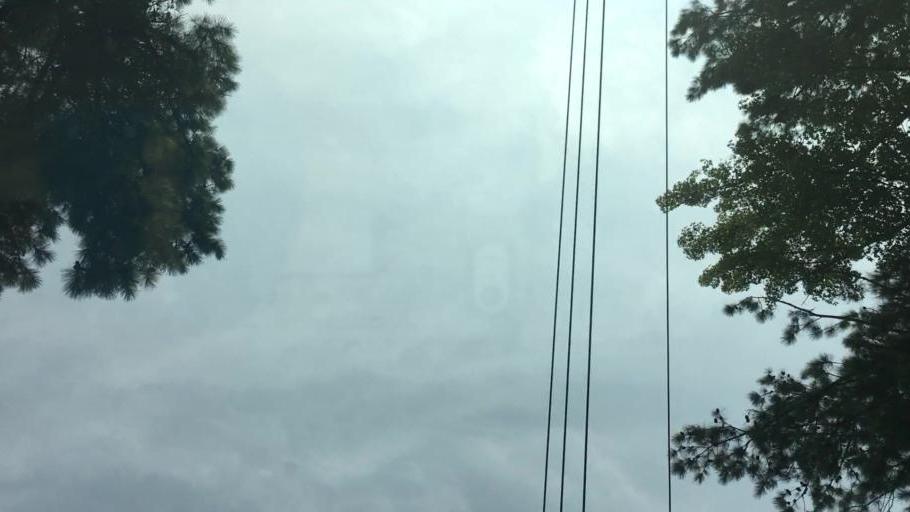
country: US
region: Alabama
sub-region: Bibb County
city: Woodstock
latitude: 33.2272
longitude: -87.1321
